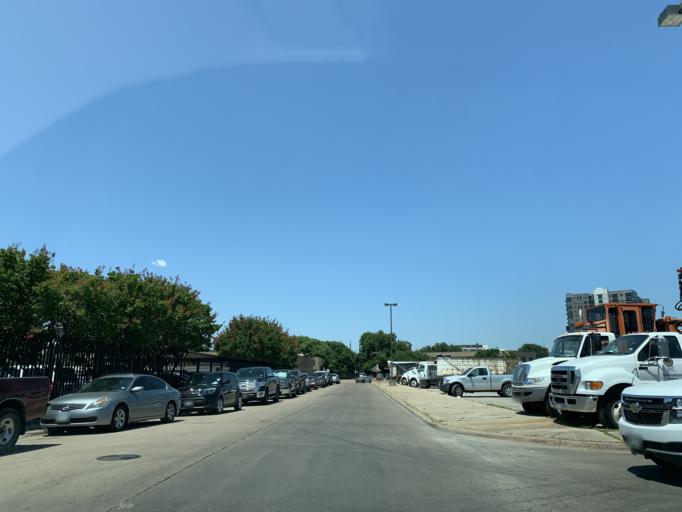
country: US
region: Texas
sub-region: Dallas County
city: Dallas
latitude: 32.7816
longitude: -96.7765
